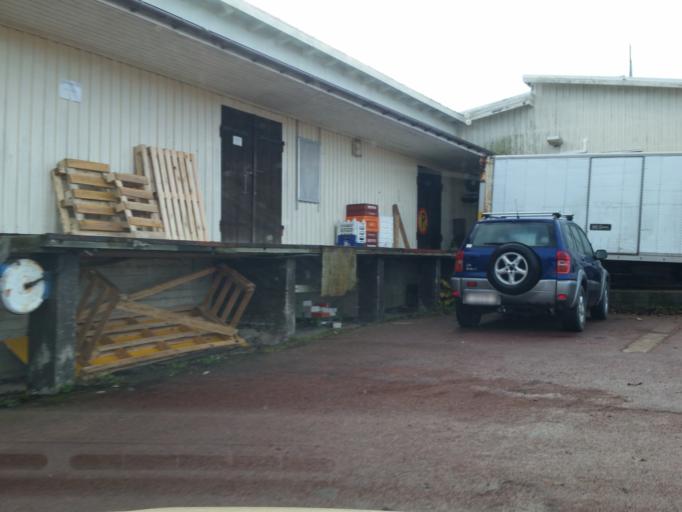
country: AX
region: Alands skaergard
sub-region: Kumlinge
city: Kumlinge
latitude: 60.2608
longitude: 20.7806
